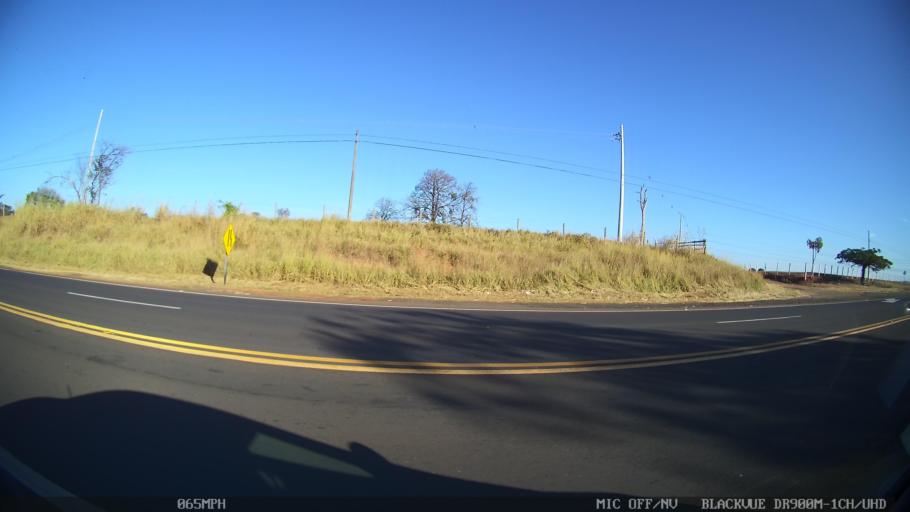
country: BR
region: Sao Paulo
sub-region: Olimpia
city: Olimpia
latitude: -20.7072
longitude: -48.9618
